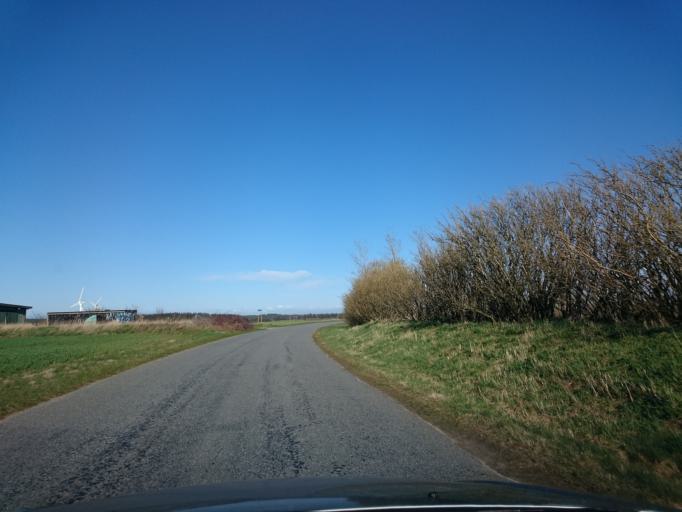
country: DK
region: North Denmark
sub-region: Hjorring Kommune
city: Hirtshals
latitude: 57.5520
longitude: 10.0485
